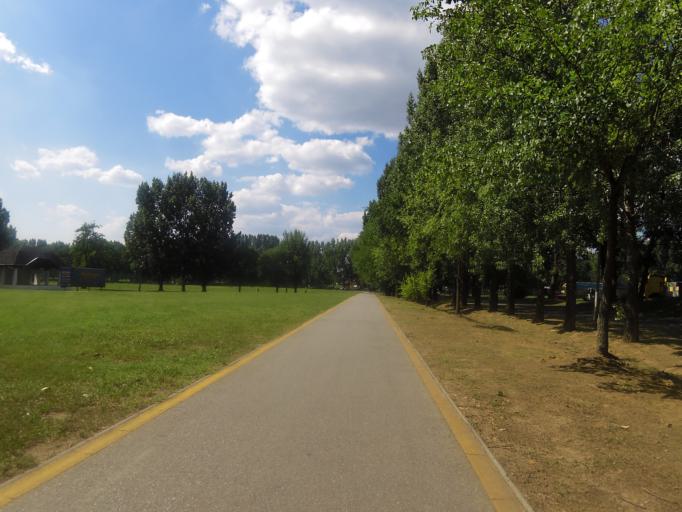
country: HU
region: Jasz-Nagykun-Szolnok
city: Tiszafured
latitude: 47.6228
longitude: 20.7375
